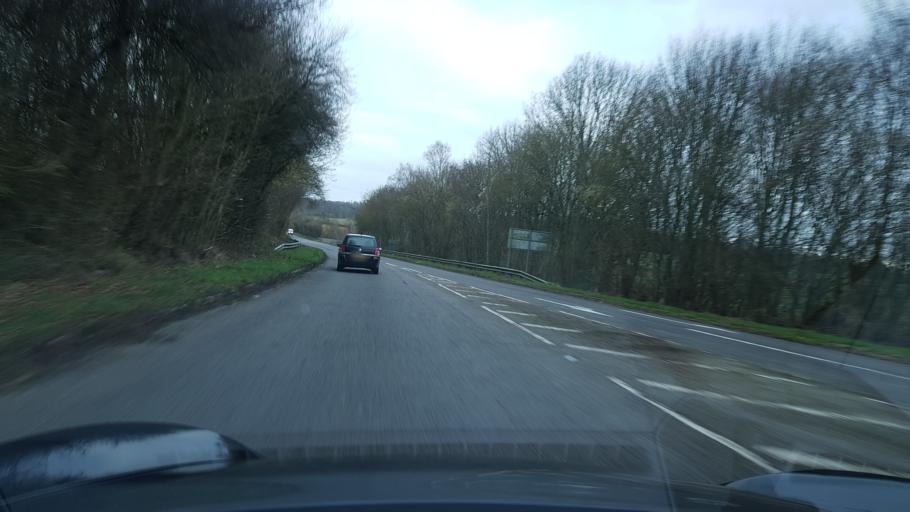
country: GB
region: England
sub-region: Hampshire
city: Kings Worthy
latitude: 51.0818
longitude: -1.1855
